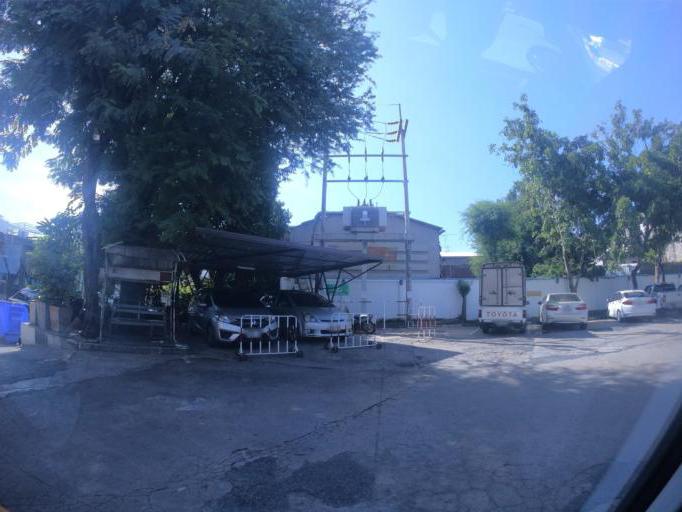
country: TH
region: Maha Sarakham
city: Chiang Yuen
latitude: 16.3729
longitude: 102.9661
